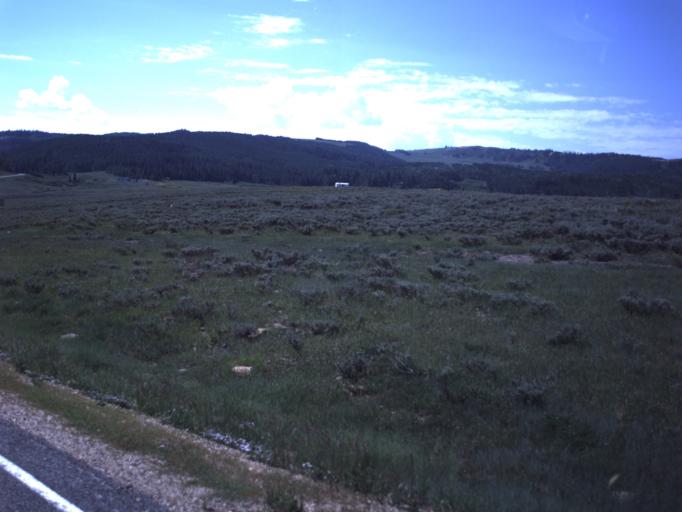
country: US
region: Utah
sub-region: Sanpete County
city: Fairview
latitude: 39.6702
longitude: -111.3078
